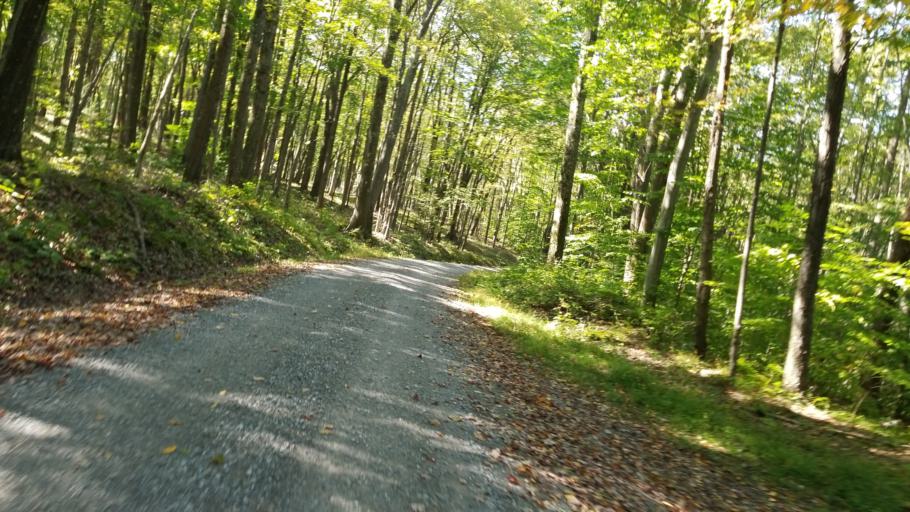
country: US
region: Pennsylvania
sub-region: Clearfield County
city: Clearfield
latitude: 41.1851
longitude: -78.5020
